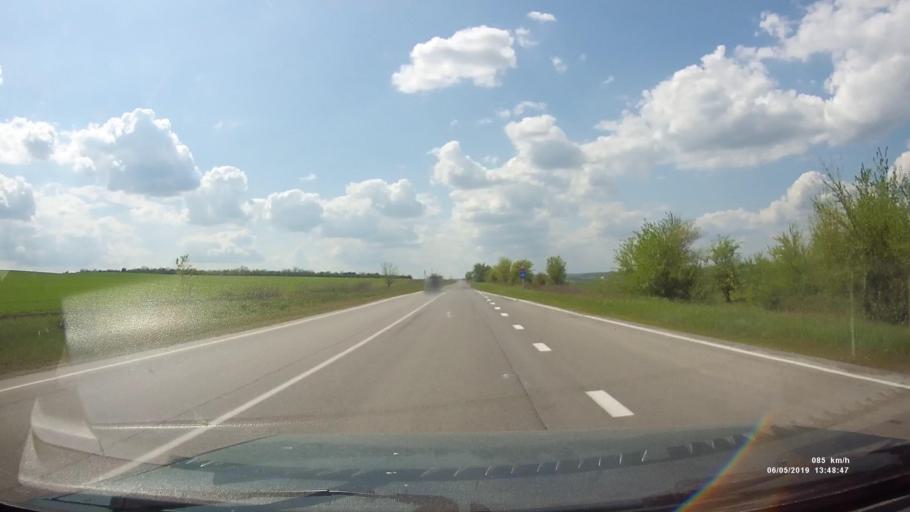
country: RU
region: Rostov
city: Melikhovskaya
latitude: 47.6589
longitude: 40.5370
